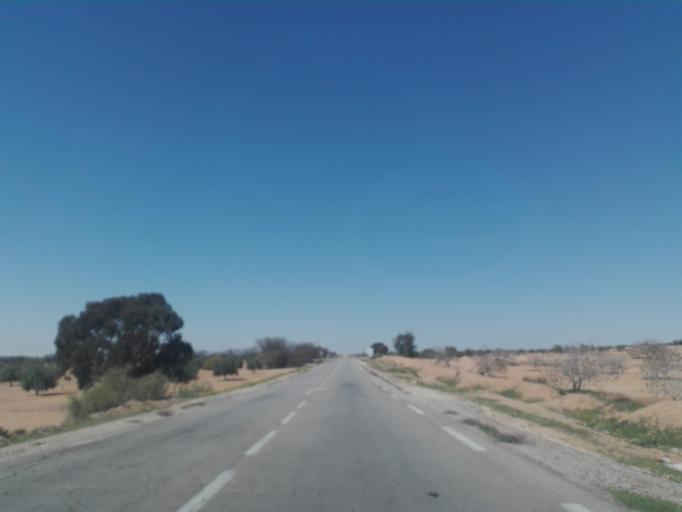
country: TN
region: Safaqis
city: Bi'r `Ali Bin Khalifah
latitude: 34.7575
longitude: 10.2737
